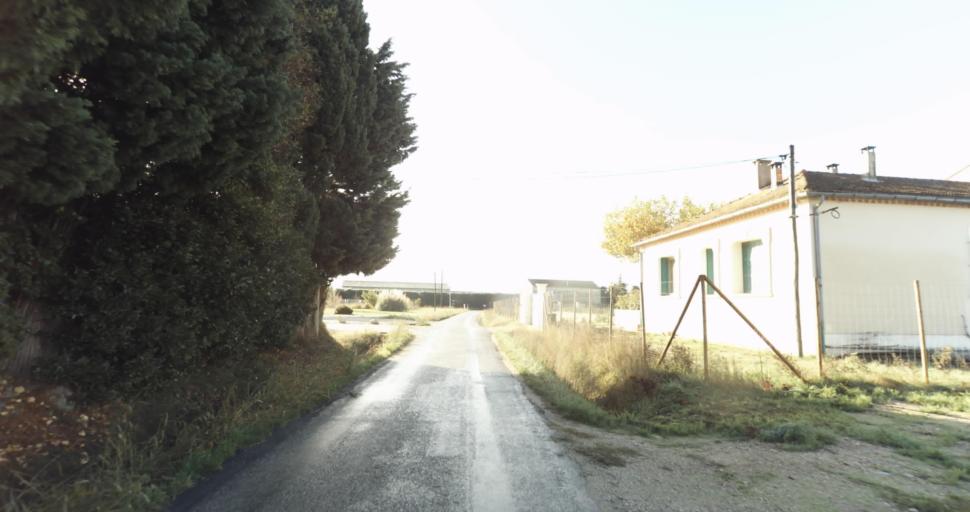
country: FR
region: Provence-Alpes-Cote d'Azur
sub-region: Departement des Bouches-du-Rhone
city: Rognonas
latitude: 43.8853
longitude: 4.7922
